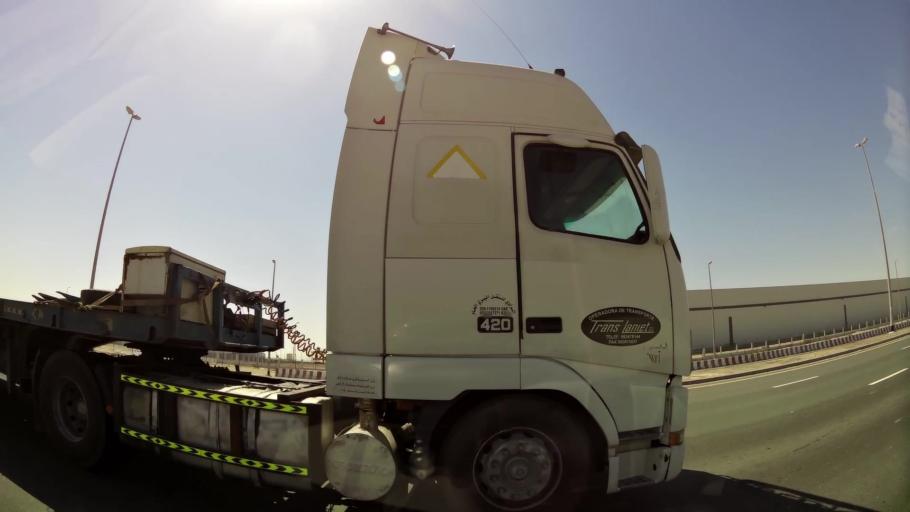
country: AE
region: Dubai
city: Dubai
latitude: 24.9651
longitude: 55.1248
